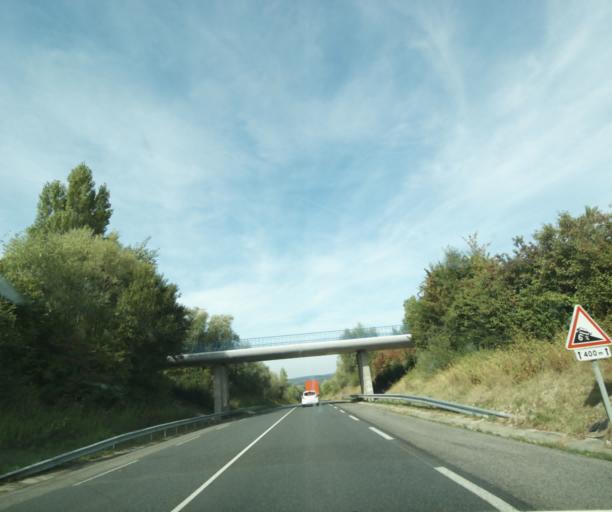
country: FR
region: Auvergne
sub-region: Departement de l'Allier
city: Saint-Germain-des-Fosses
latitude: 46.1897
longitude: 3.4366
